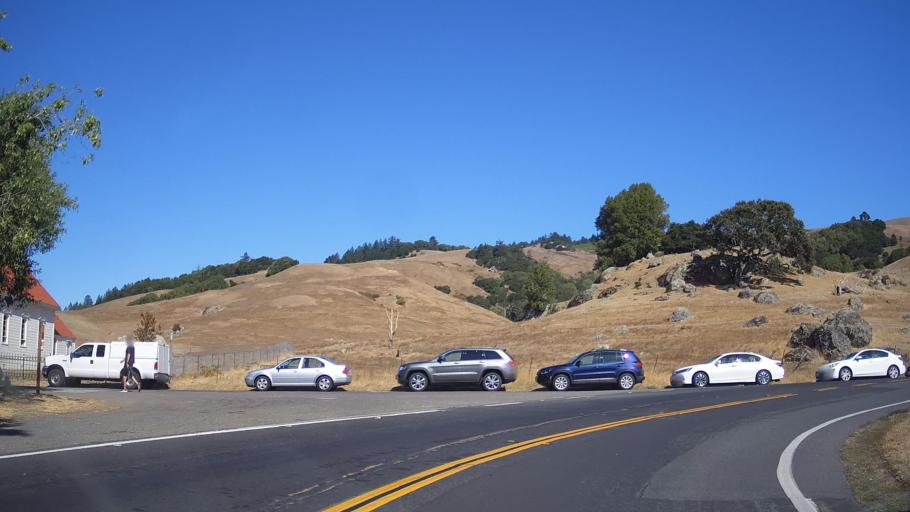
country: US
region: California
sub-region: Marin County
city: Lagunitas-Forest Knolls
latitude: 38.0608
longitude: -122.6981
